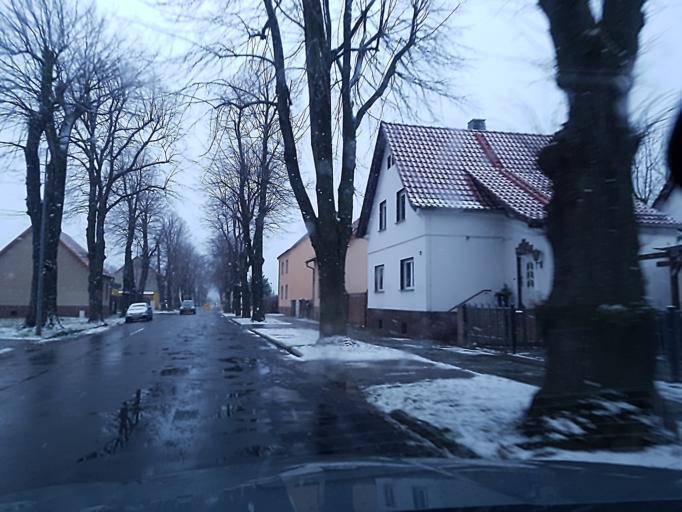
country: DE
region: Brandenburg
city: Elsterwerda
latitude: 51.4485
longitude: 13.5289
